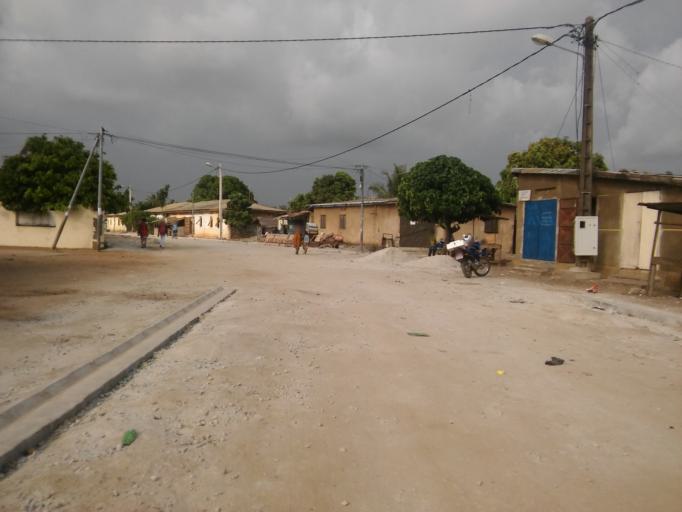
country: CI
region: Sud-Comoe
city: Grand-Bassam
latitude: 5.2071
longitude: -3.7310
